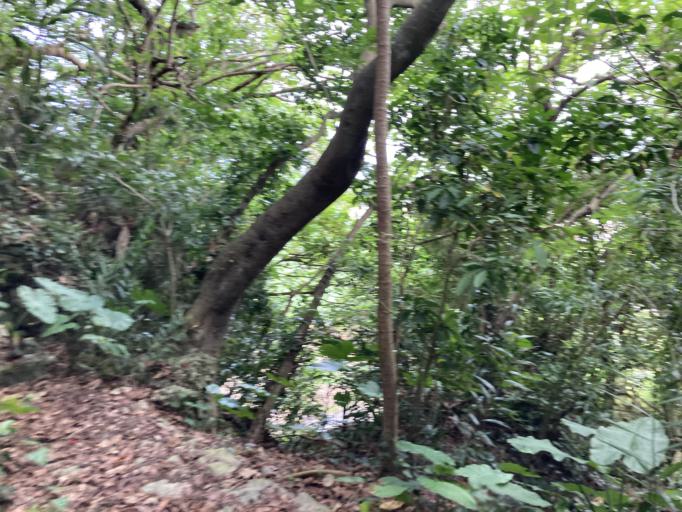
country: JP
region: Okinawa
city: Tomigusuku
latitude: 26.1378
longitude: 127.7929
